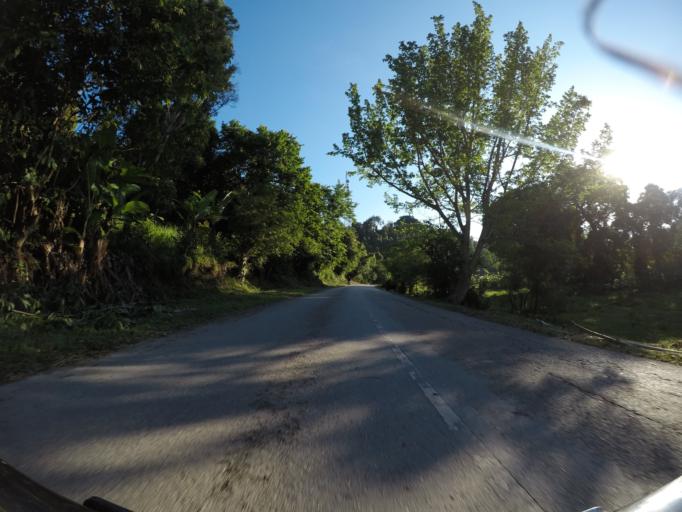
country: TZ
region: Pemba South
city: Mtambile
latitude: -5.3755
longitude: 39.6929
